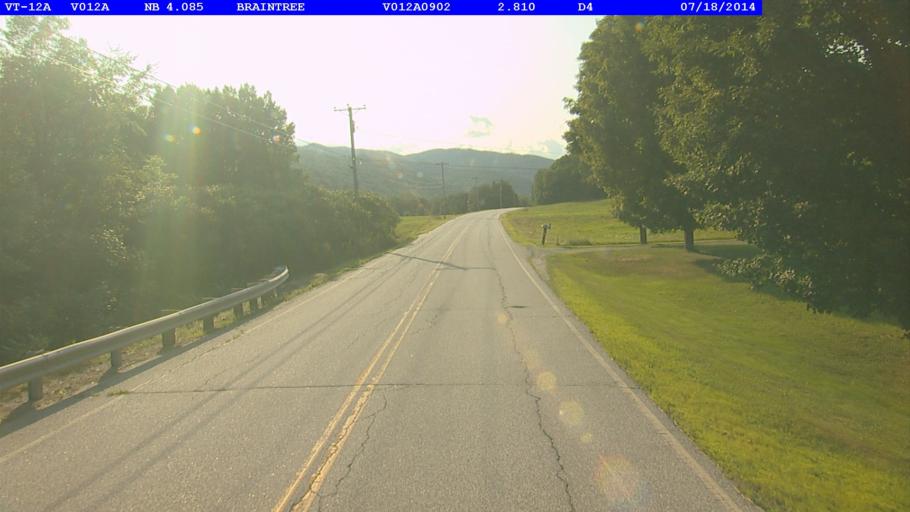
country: US
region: Vermont
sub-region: Orange County
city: Randolph
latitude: 43.9555
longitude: -72.7251
